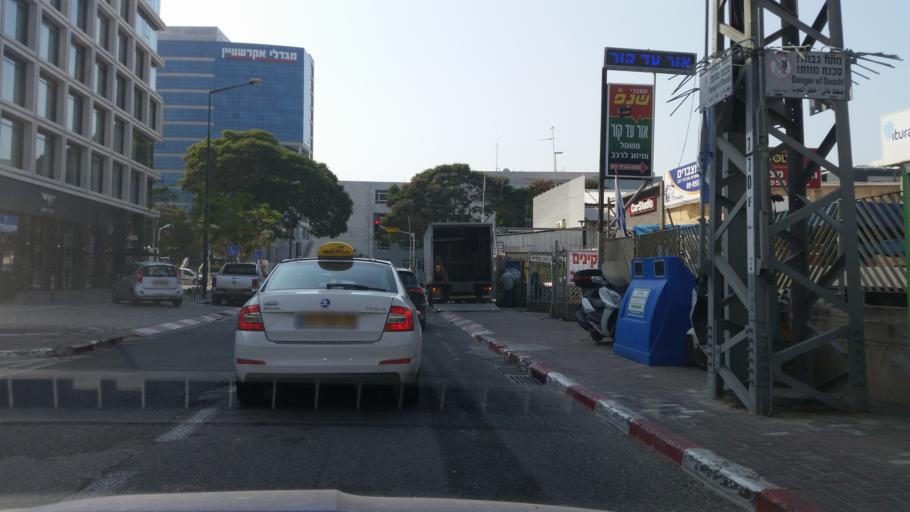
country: IL
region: Tel Aviv
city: Herzliya Pituah
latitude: 32.1631
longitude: 34.8082
